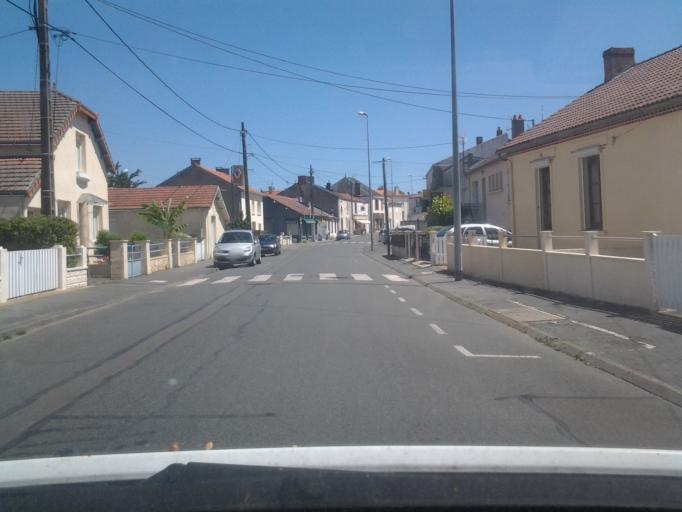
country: FR
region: Pays de la Loire
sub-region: Departement de la Vendee
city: La Roche-sur-Yon
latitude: 46.6620
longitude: -1.4038
